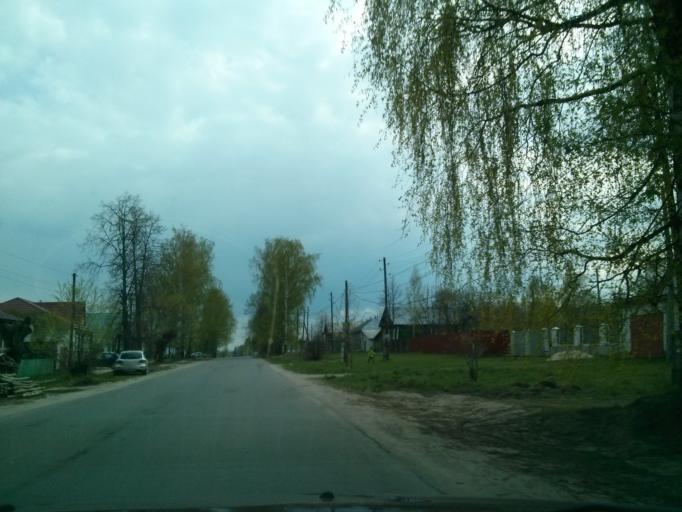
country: RU
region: Nizjnij Novgorod
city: Shimorskoye
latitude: 55.3415
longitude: 41.9290
